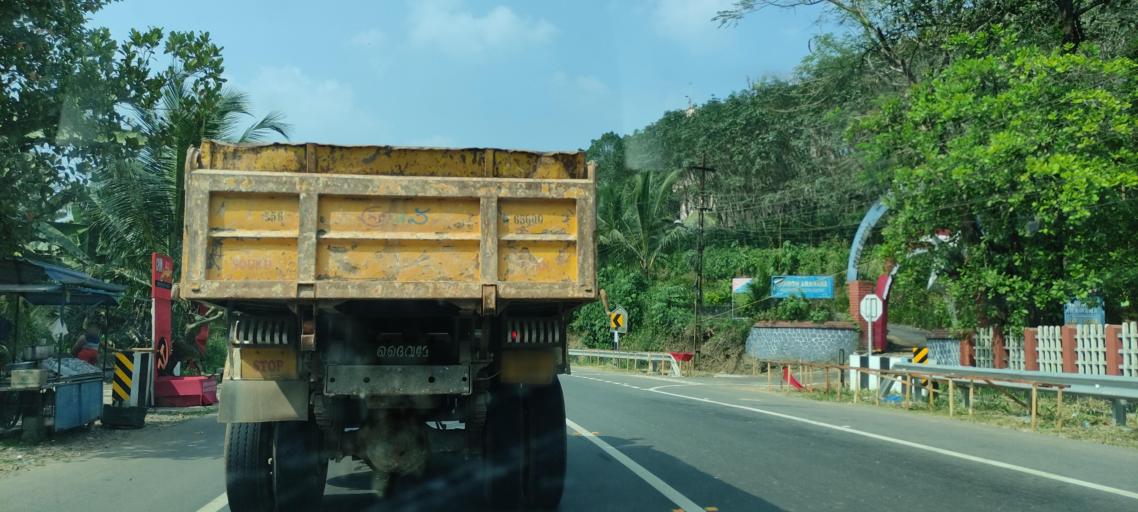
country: IN
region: Kerala
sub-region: Pattanamtitta
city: Adur
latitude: 9.1654
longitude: 76.7191
